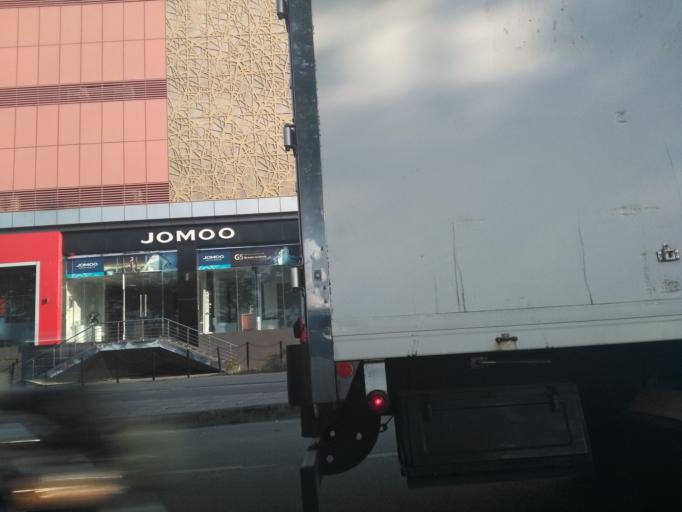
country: TZ
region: Dar es Salaam
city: Dar es Salaam
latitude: -6.8292
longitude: 39.2739
